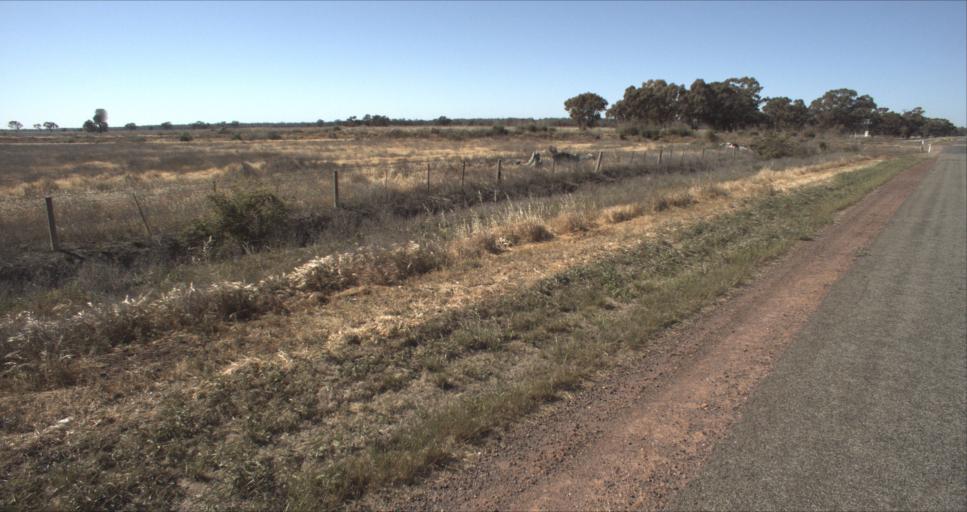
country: AU
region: New South Wales
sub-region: Leeton
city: Leeton
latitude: -34.5872
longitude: 146.2604
